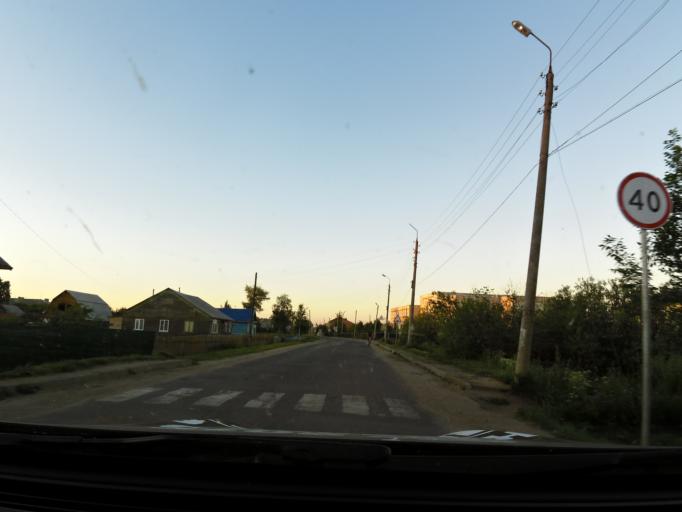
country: RU
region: Jaroslavl
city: Lyubim
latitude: 58.3565
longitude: 40.6932
